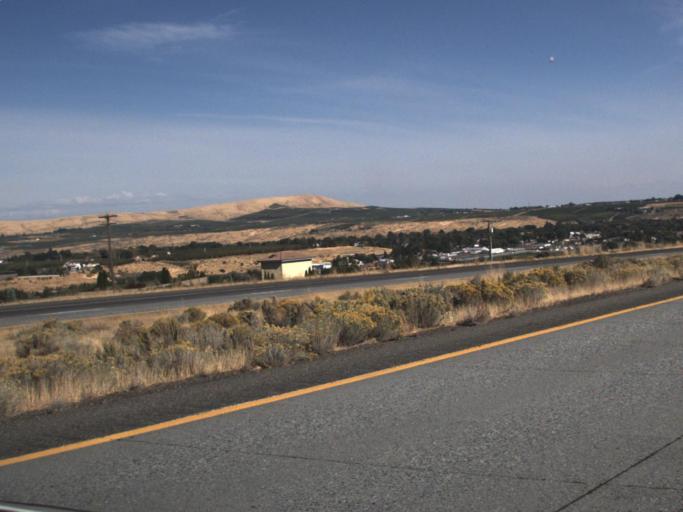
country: US
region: Washington
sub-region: Benton County
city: Benton City
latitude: 46.2602
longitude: -119.5168
